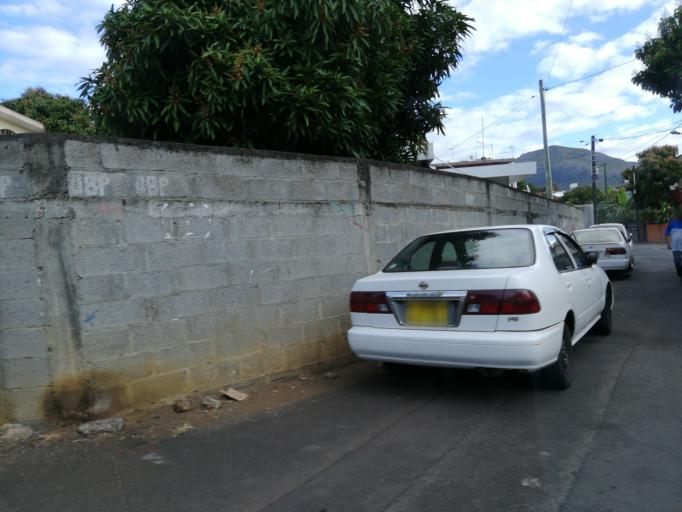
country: MU
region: Plaines Wilhems
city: Ebene
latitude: -20.2343
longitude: 57.4617
